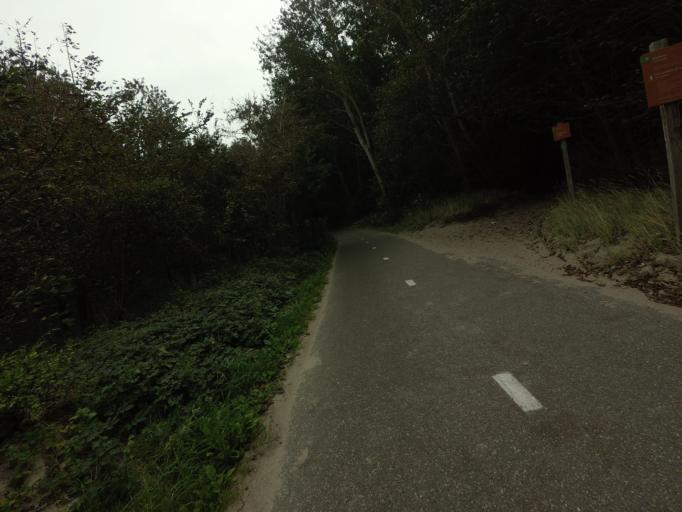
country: NL
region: Zeeland
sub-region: Gemeente Vlissingen
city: Vlissingen
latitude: 51.4938
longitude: 3.5010
